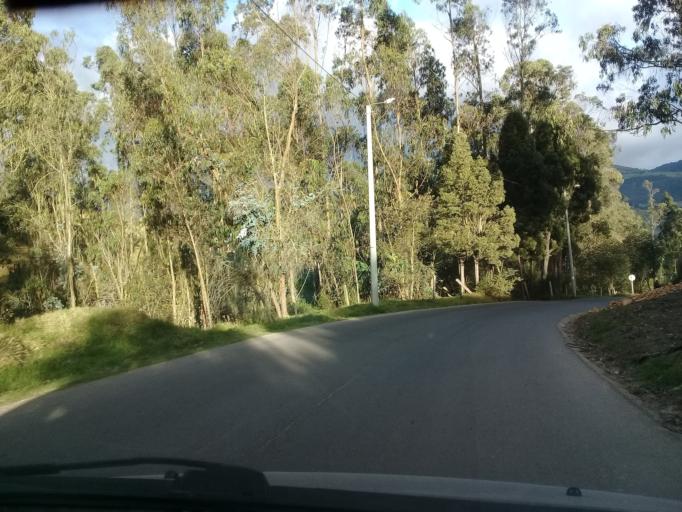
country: CO
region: Cundinamarca
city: Villapinzon
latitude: 5.2207
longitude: -73.6043
